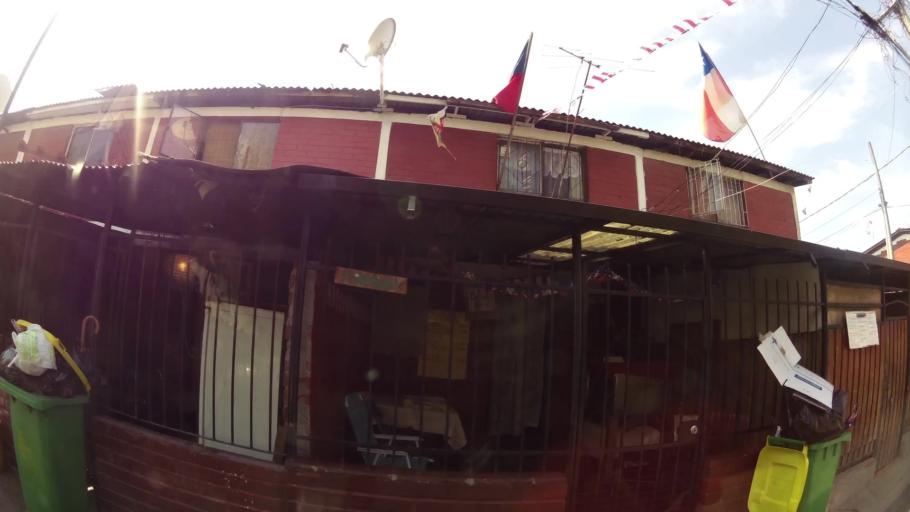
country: CL
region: Santiago Metropolitan
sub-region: Provincia de Santiago
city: La Pintana
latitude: -33.5592
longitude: -70.6513
